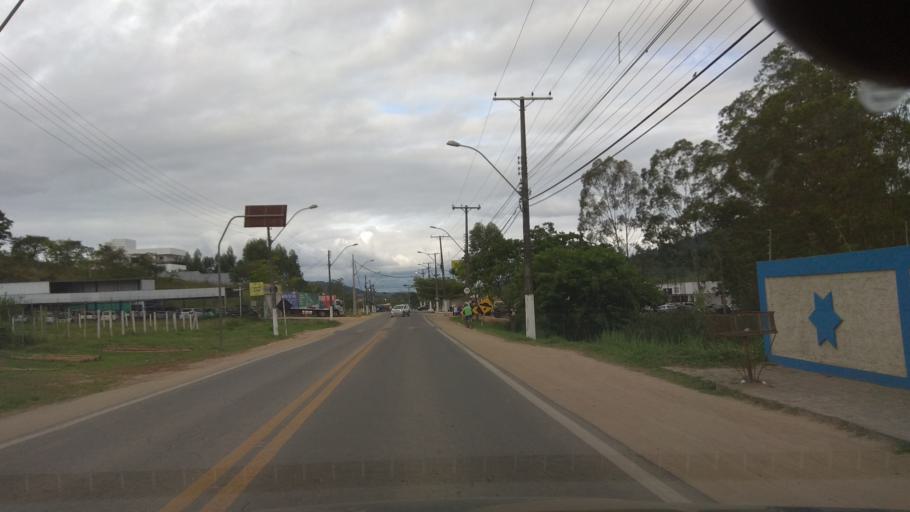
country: BR
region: Bahia
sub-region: Ipiau
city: Ipiau
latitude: -14.1400
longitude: -39.7289
